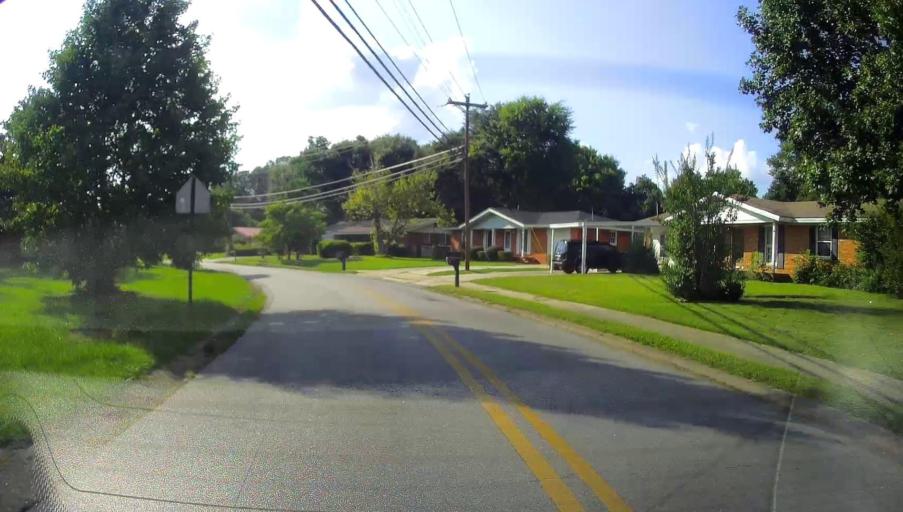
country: US
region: Georgia
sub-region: Houston County
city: Centerville
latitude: 32.6012
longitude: -83.6541
